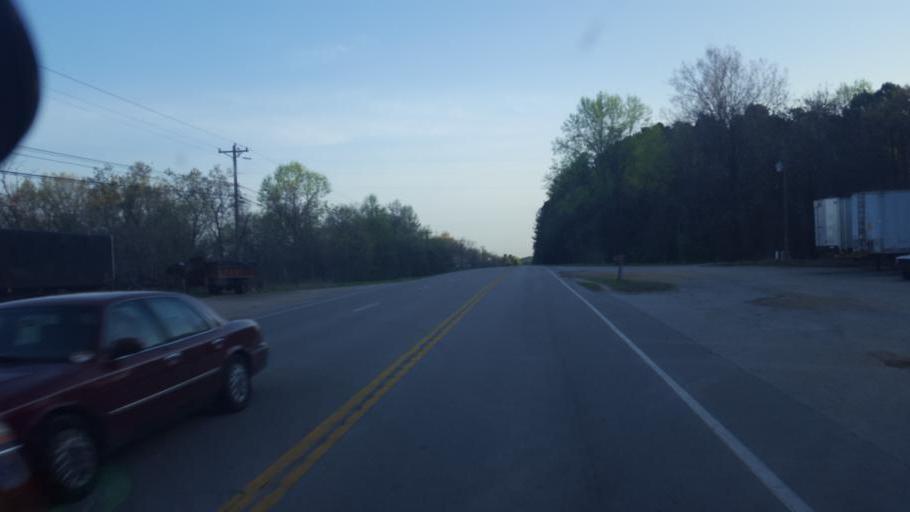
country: US
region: Kentucky
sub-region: Hart County
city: Munfordville
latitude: 37.3226
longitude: -85.9093
